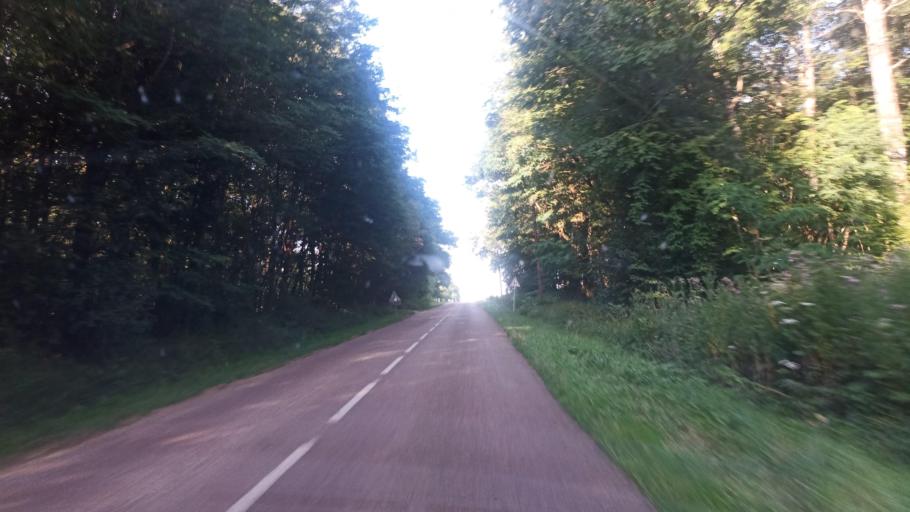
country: FR
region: Bourgogne
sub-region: Departement de l'Yonne
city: Pont-sur-Yonne
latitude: 48.2408
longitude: 3.1421
